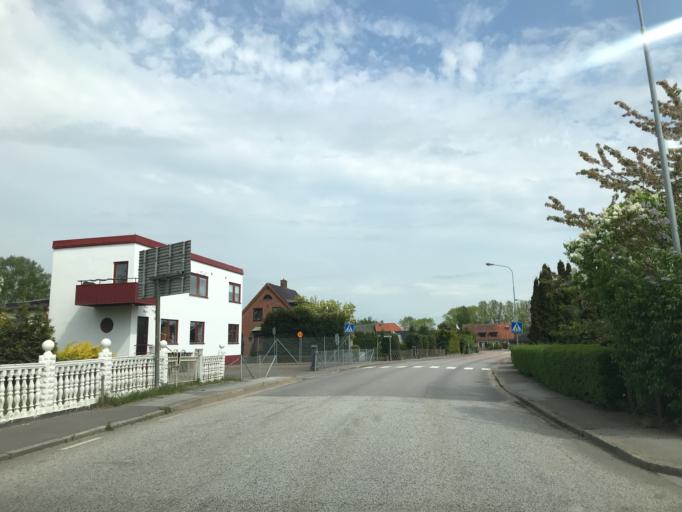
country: SE
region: Skane
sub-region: Svalovs Kommun
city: Teckomatorp
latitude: 55.8630
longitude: 13.1457
